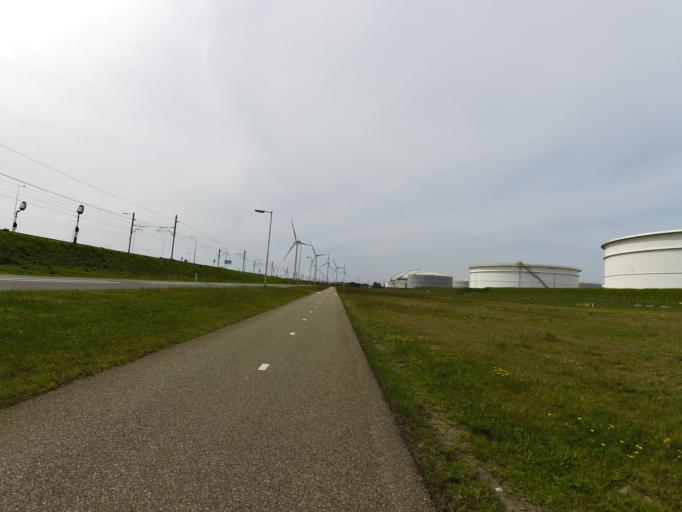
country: NL
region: South Holland
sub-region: Gemeente Maassluis
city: Maassluis
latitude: 51.9042
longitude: 4.2132
